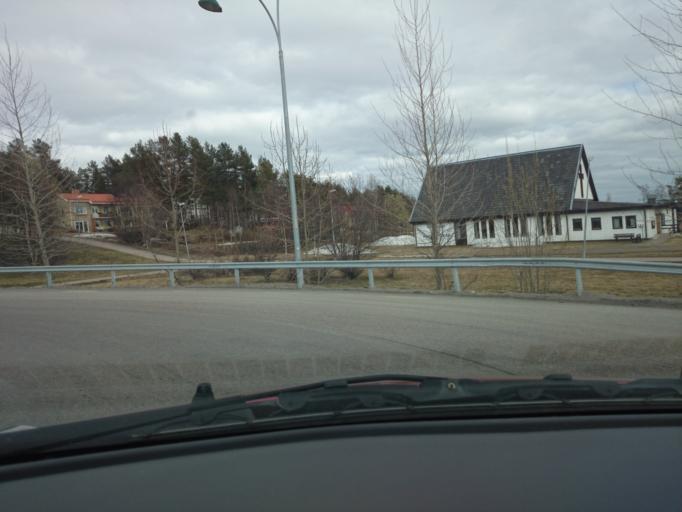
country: SE
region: Norrbotten
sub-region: Gallivare Kommun
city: Gaellivare
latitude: 67.1384
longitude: 20.6608
